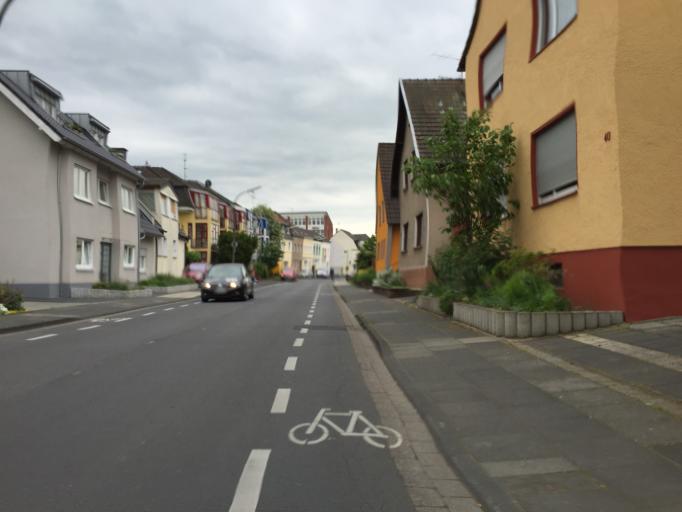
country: DE
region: North Rhine-Westphalia
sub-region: Regierungsbezirk Koln
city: Bonn
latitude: 50.7157
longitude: 7.0711
